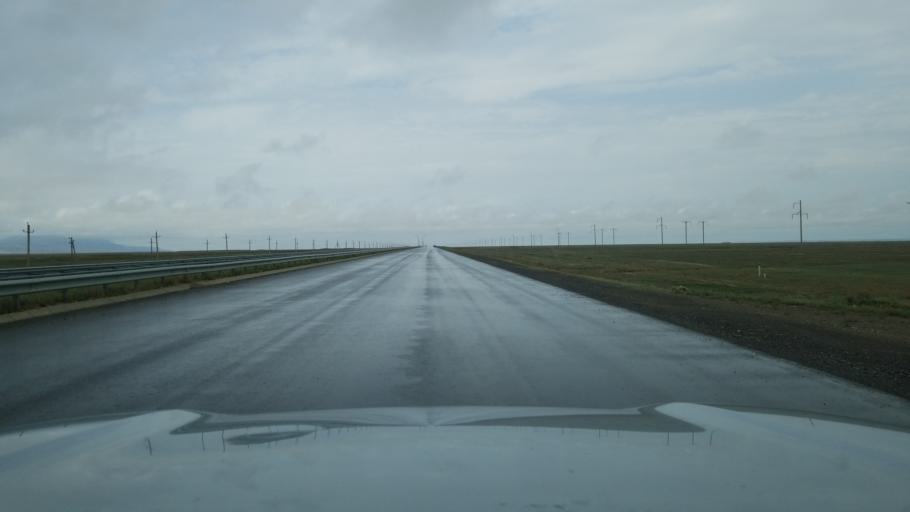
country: TM
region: Balkan
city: Gazanjyk
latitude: 39.1524
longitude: 55.8525
